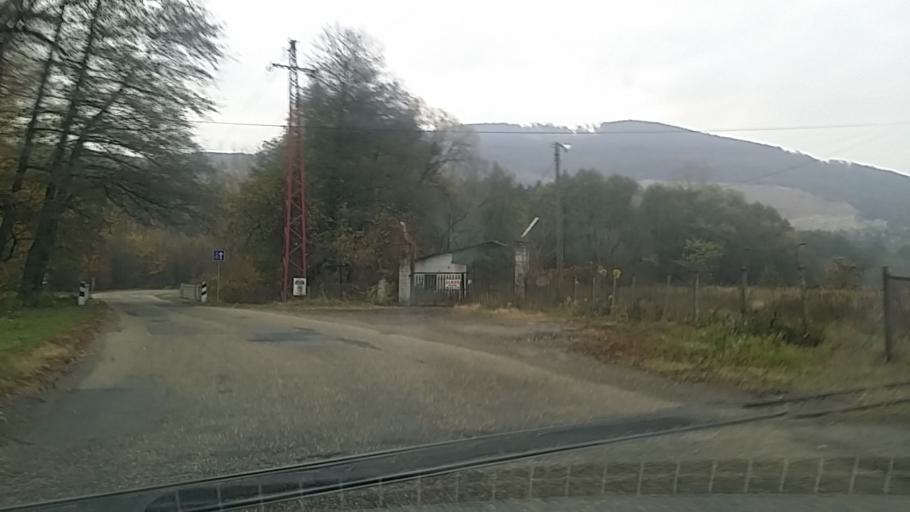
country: HU
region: Borsod-Abauj-Zemplen
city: Sarospatak
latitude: 48.4662
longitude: 21.4961
